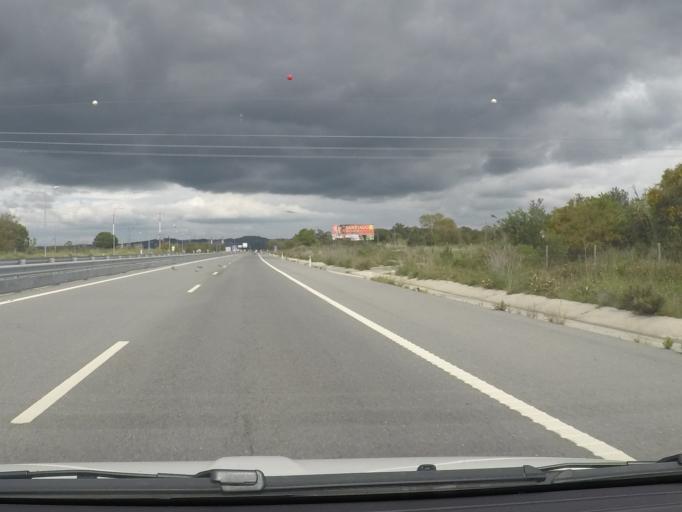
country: PT
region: Setubal
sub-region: Santiago do Cacem
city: Santo Andre
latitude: 37.9955
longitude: -8.7597
